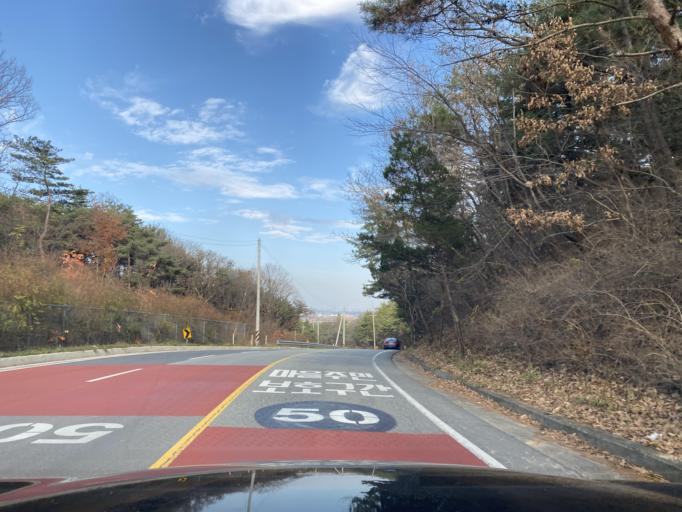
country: KR
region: Chungcheongnam-do
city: Hongsung
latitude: 36.6671
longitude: 126.6371
